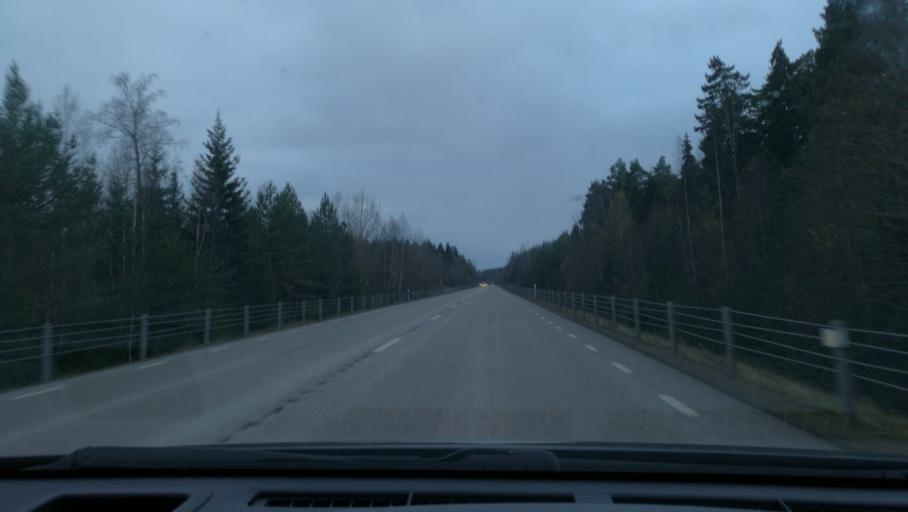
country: SE
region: Soedermanland
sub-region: Eskilstuna Kommun
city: Kvicksund
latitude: 59.5134
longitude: 16.3167
